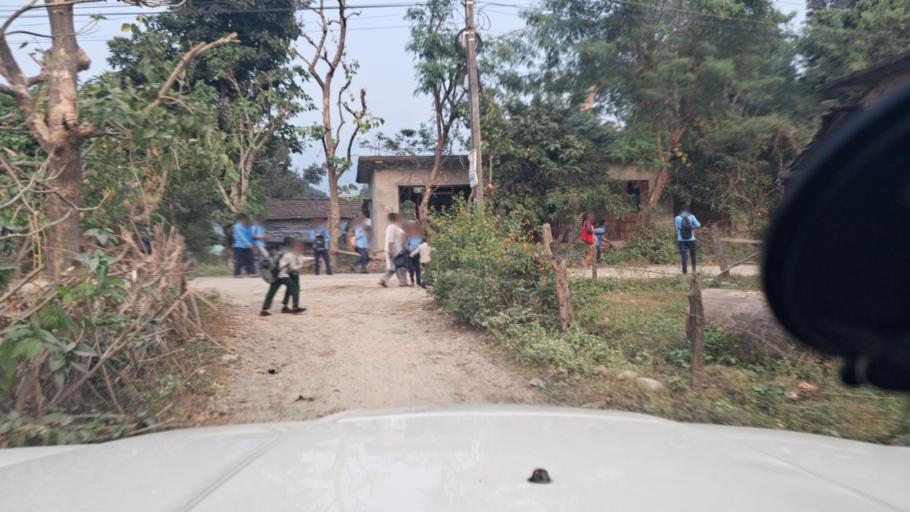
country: IN
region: Uttarakhand
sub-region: Udham Singh Nagar
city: Tanakpur
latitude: 29.0604
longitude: 80.1377
